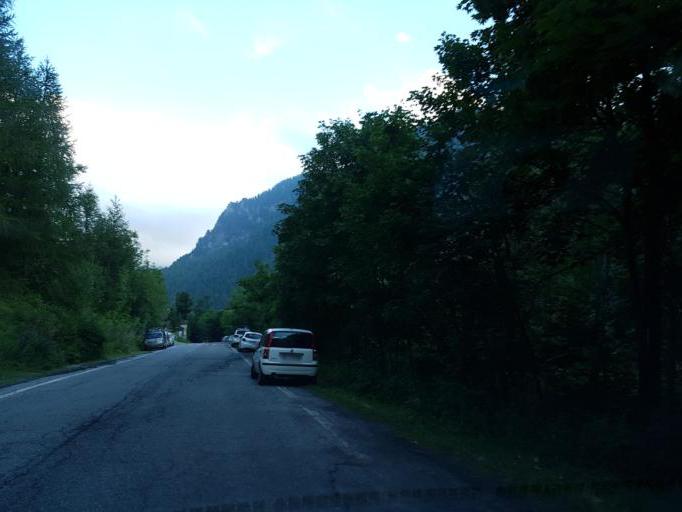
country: IT
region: Piedmont
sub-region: Provincia di Cuneo
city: Pontechianale
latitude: 44.6144
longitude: 7.0526
